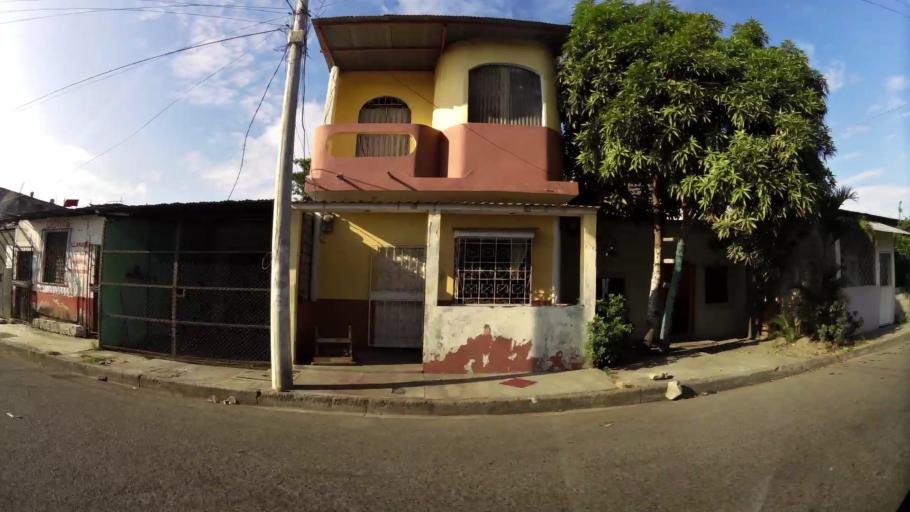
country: EC
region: Guayas
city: Guayaquil
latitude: -2.2157
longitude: -79.9215
